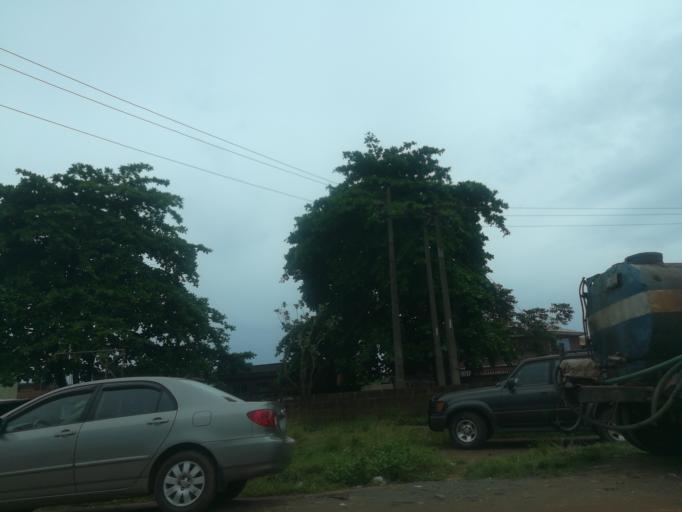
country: NG
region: Oyo
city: Ibadan
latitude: 7.3915
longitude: 3.9672
